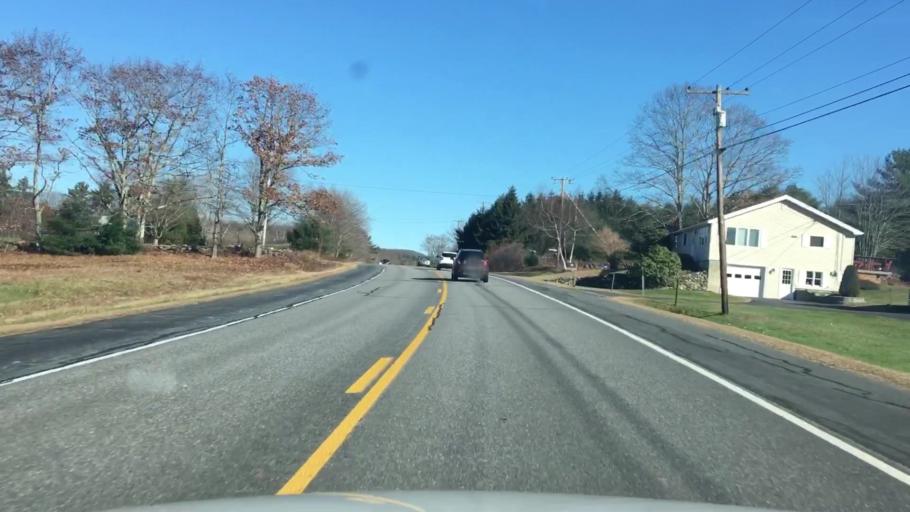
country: US
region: Maine
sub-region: Knox County
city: Union
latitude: 44.2122
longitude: -69.2101
